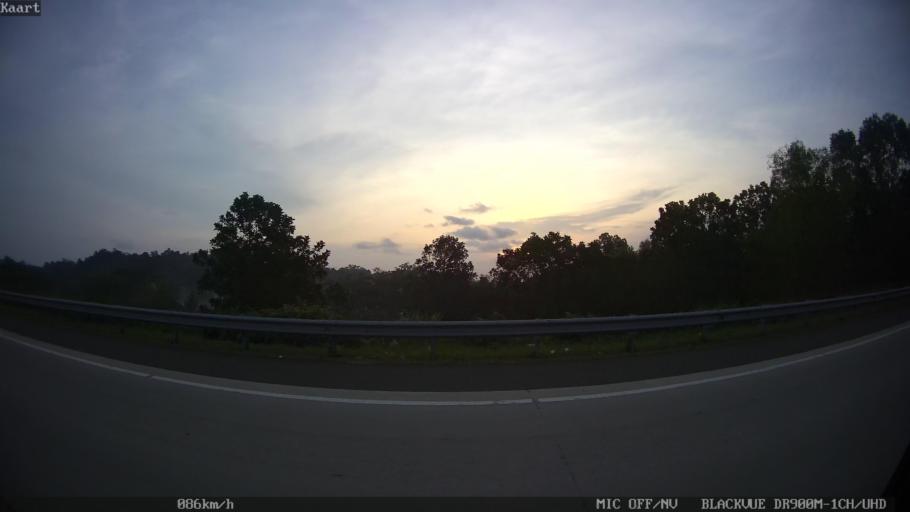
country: ID
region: Lampung
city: Penengahan
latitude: -5.8469
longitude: 105.7270
